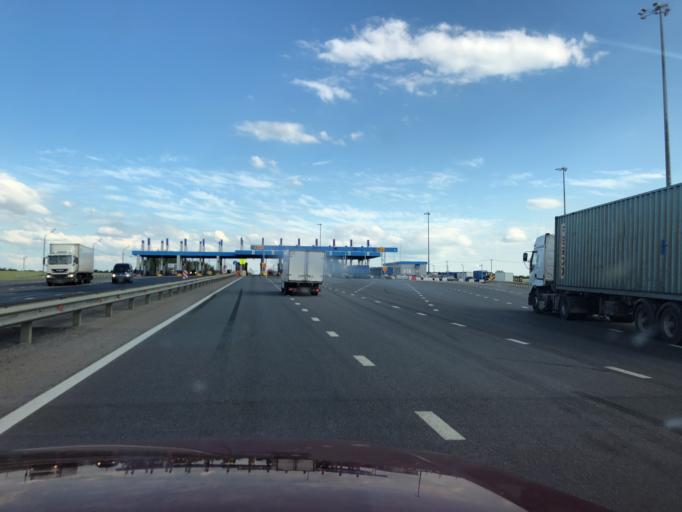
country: RU
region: Lipetsk
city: Zadonsk
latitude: 52.4314
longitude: 38.8231
